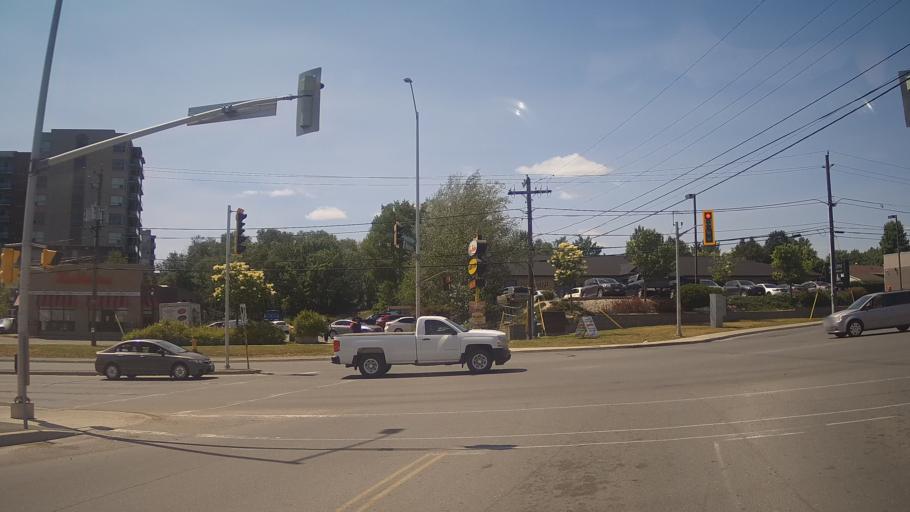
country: CA
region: Ontario
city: Greater Sudbury
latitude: 46.4635
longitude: -81.0079
